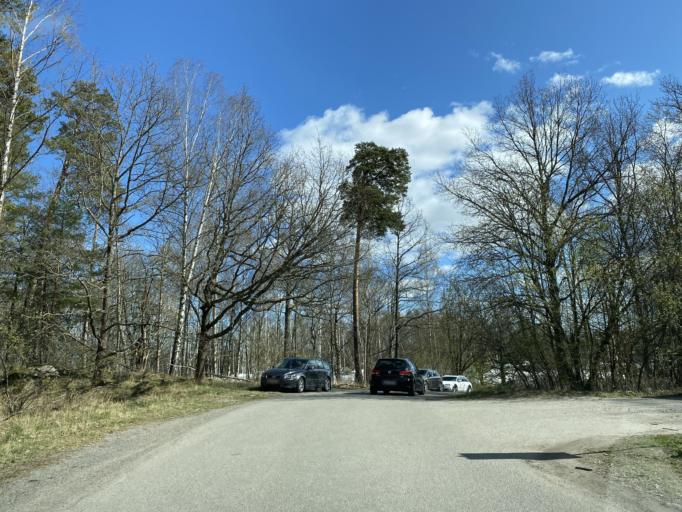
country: SE
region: Stockholm
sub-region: Nacka Kommun
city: Nacka
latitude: 59.3301
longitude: 18.1487
